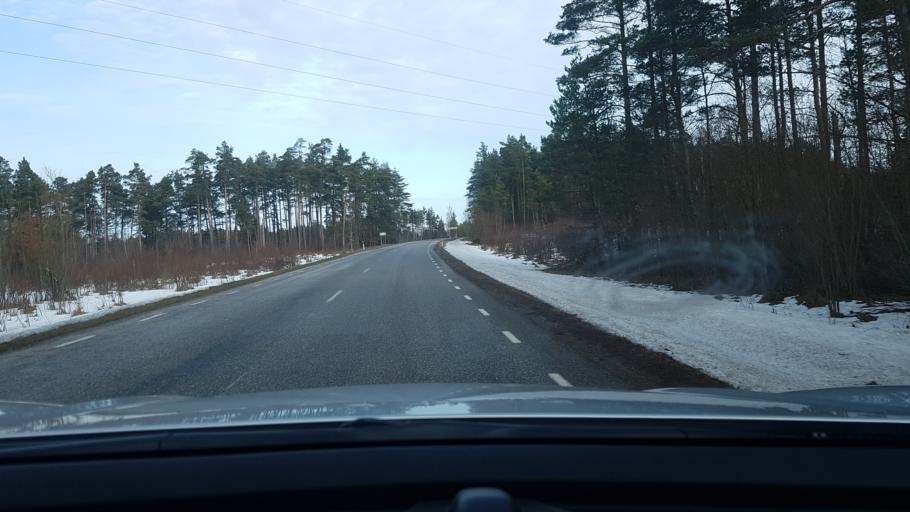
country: EE
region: Saare
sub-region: Kuressaare linn
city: Kuressaare
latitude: 58.4398
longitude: 22.7048
